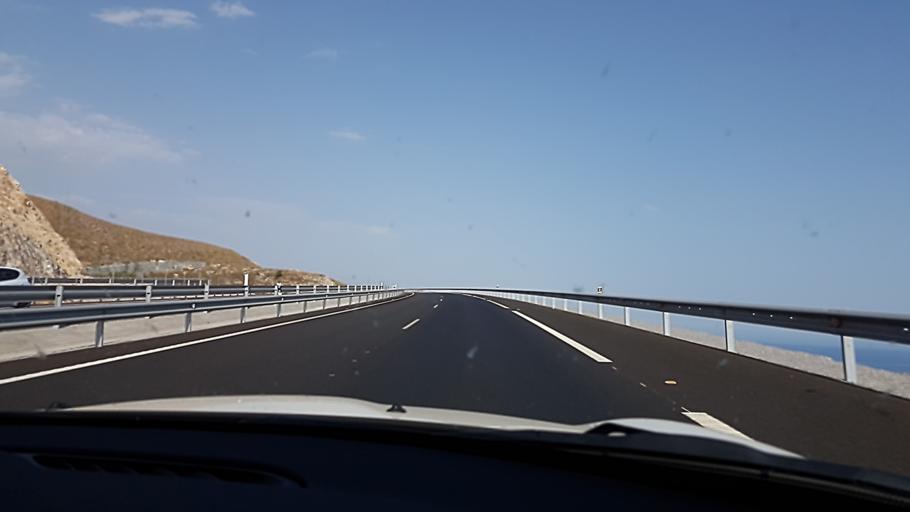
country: ES
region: Andalusia
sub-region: Provincia de Granada
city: Gualchos
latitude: 36.7154
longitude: -3.3850
